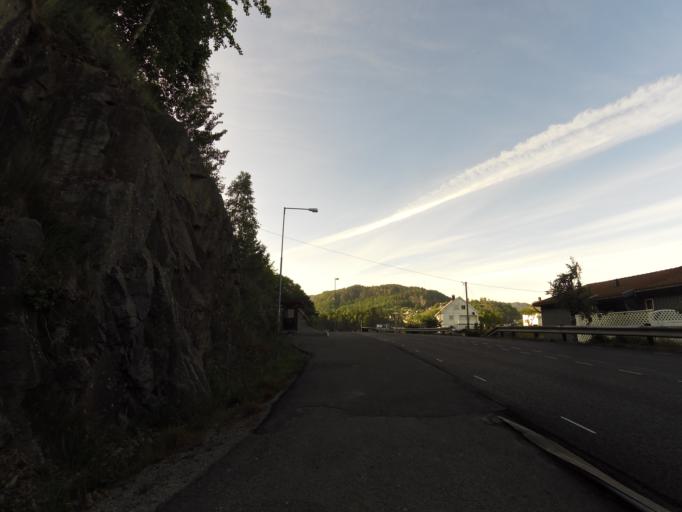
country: NO
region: Vest-Agder
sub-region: Flekkefjord
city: Flekkefjord
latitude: 58.2902
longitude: 6.6486
